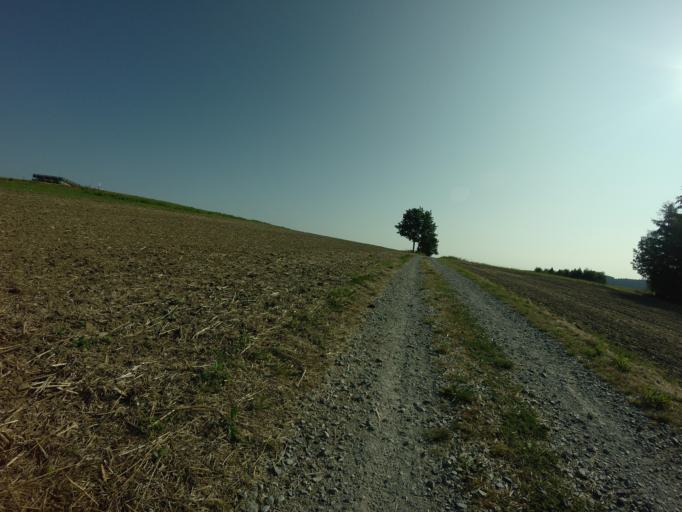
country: AT
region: Upper Austria
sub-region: Politischer Bezirk Urfahr-Umgebung
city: Bad Leonfelden
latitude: 48.5272
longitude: 14.3035
